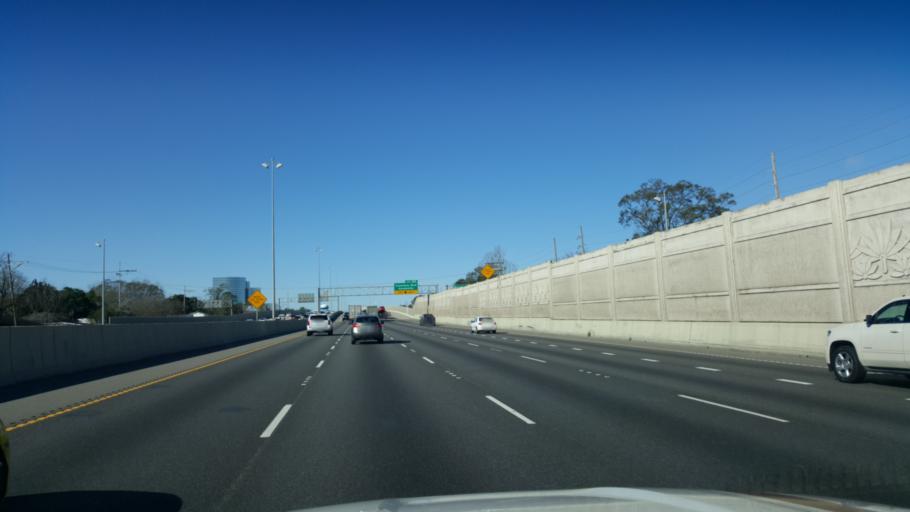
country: US
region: Louisiana
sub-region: Jefferson Parish
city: Metairie Terrace
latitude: 30.0049
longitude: -90.1822
